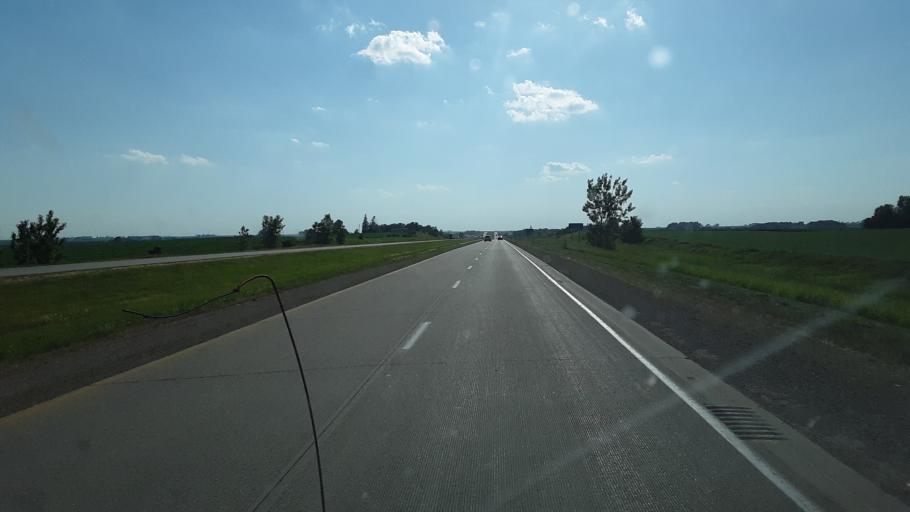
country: US
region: Iowa
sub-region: Grundy County
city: Grundy Center
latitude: 42.4631
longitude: -92.7412
